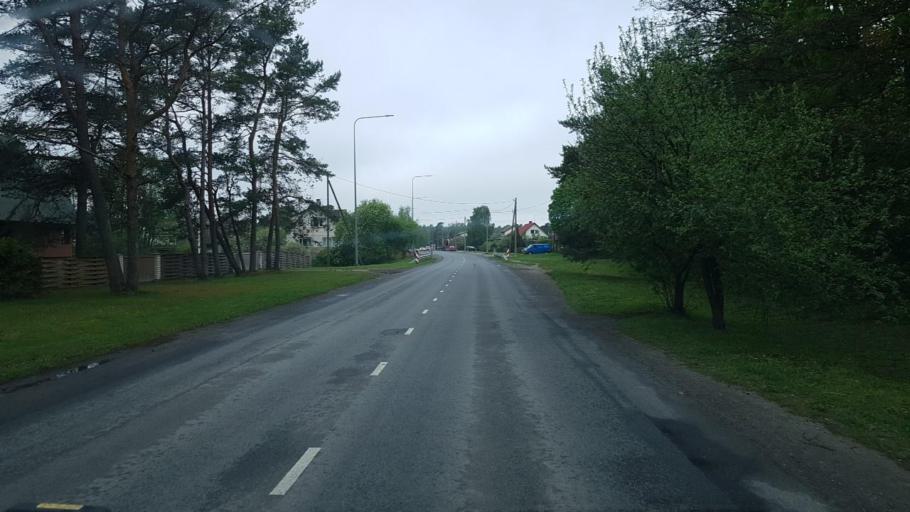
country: EE
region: Laeaene
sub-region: Haapsalu linn
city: Haapsalu
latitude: 58.9292
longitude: 23.5341
